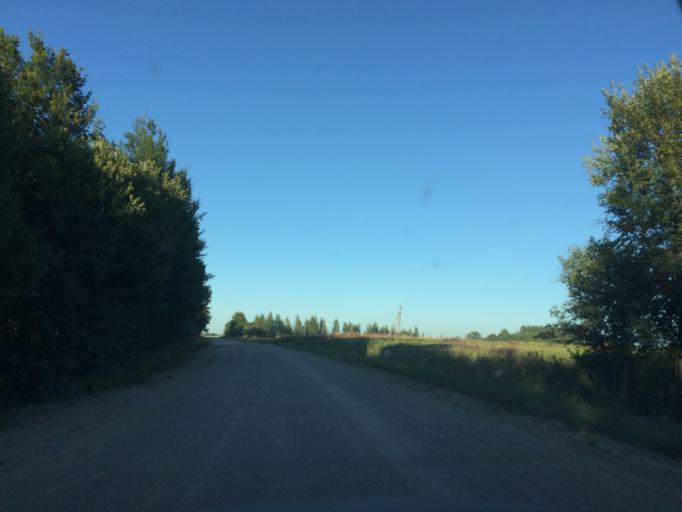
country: LV
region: Rezekne
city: Rezekne
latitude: 56.6161
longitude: 27.4622
